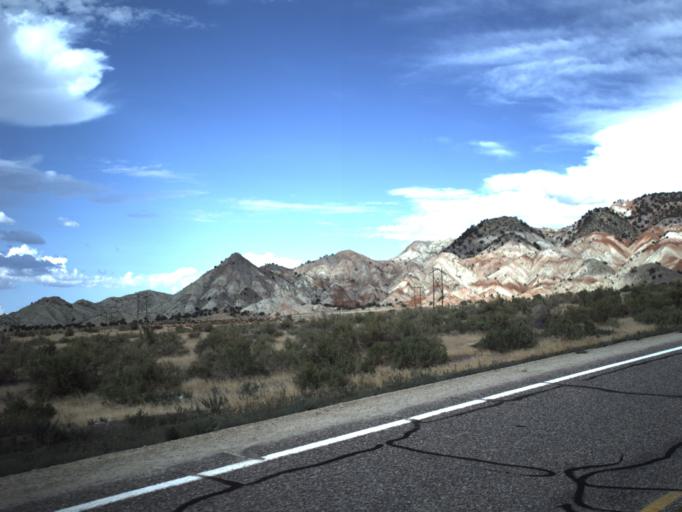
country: US
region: Utah
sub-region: Sevier County
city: Richfield
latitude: 38.7747
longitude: -111.9561
